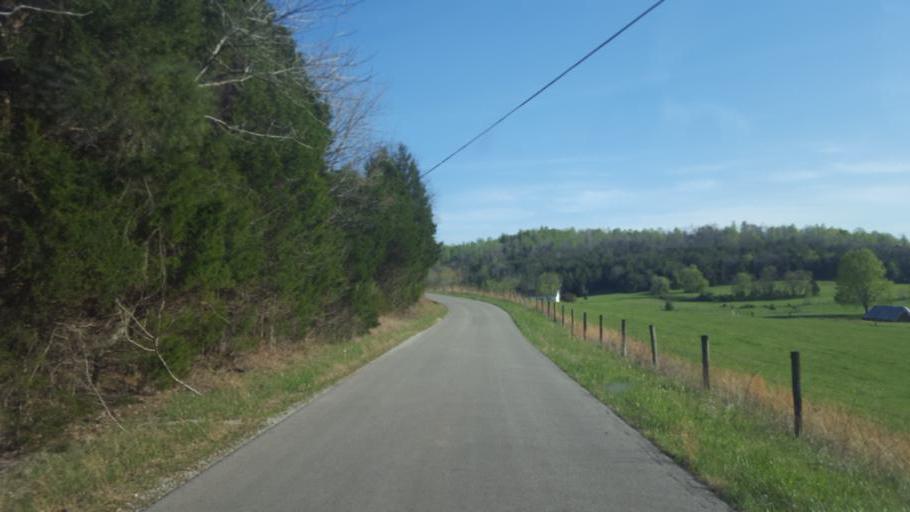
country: US
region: Kentucky
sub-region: Barren County
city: Cave City
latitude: 37.1827
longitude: -86.0100
